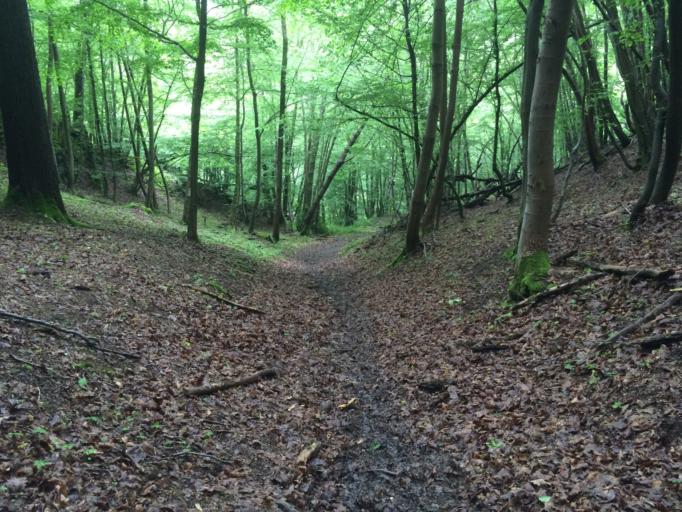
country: BE
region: Wallonia
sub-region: Province de Namur
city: Yvoir
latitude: 50.3262
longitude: 4.9401
